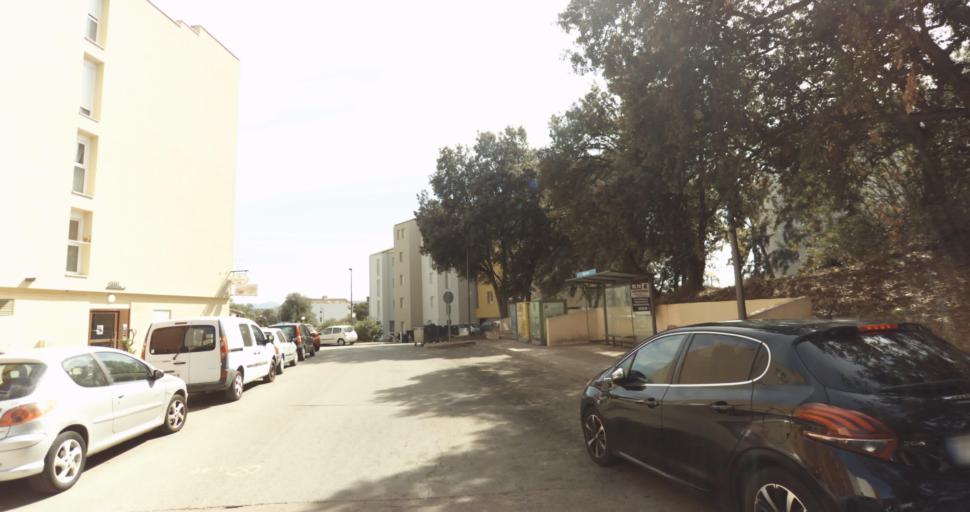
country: FR
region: Corsica
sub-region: Departement de la Corse-du-Sud
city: Ajaccio
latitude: 41.9480
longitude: 8.7533
